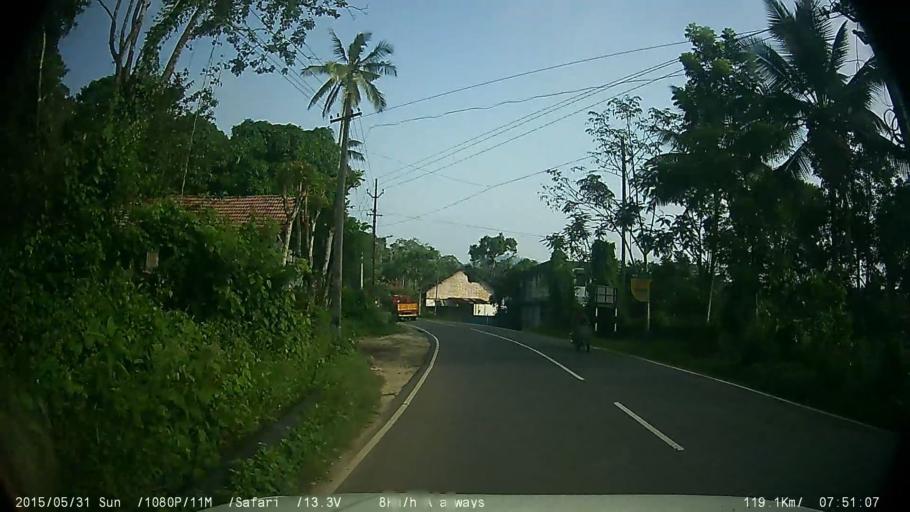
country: IN
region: Kerala
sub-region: Wayanad
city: Kalpetta
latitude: 11.6342
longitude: 76.0889
